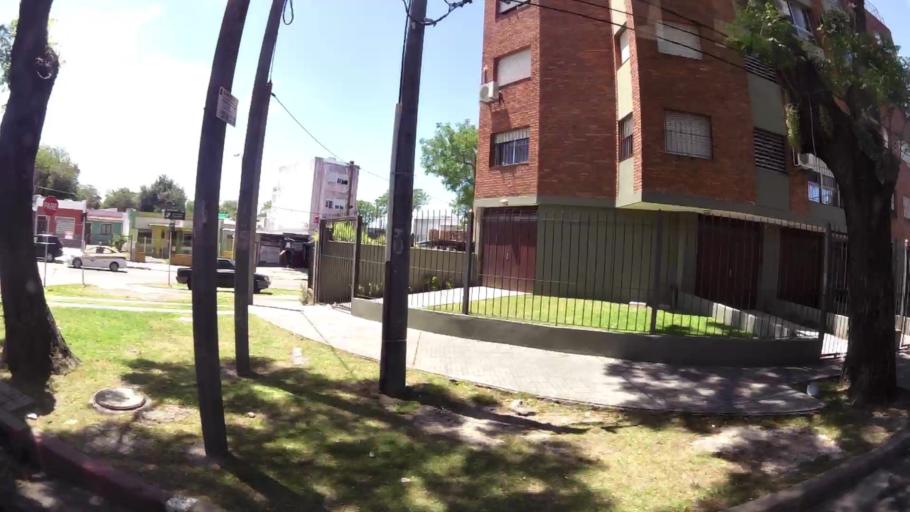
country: UY
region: Montevideo
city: Montevideo
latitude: -34.8907
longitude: -56.1266
